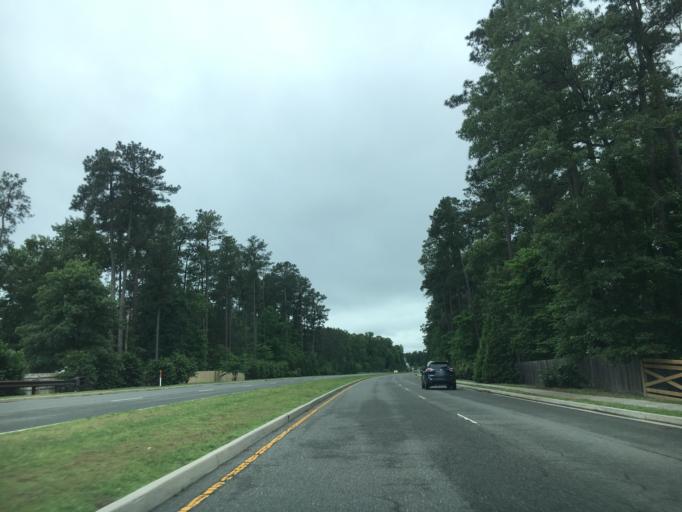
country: US
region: Virginia
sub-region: Henrico County
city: Short Pump
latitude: 37.6266
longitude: -77.6167
